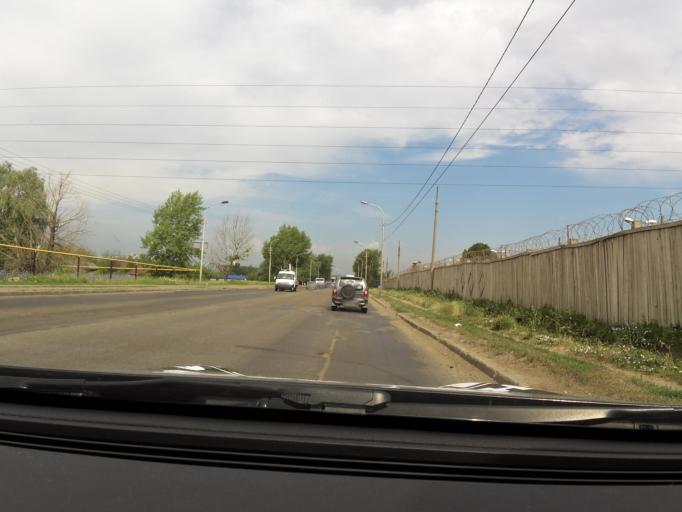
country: RU
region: Bashkortostan
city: Iglino
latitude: 54.7833
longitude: 56.2232
